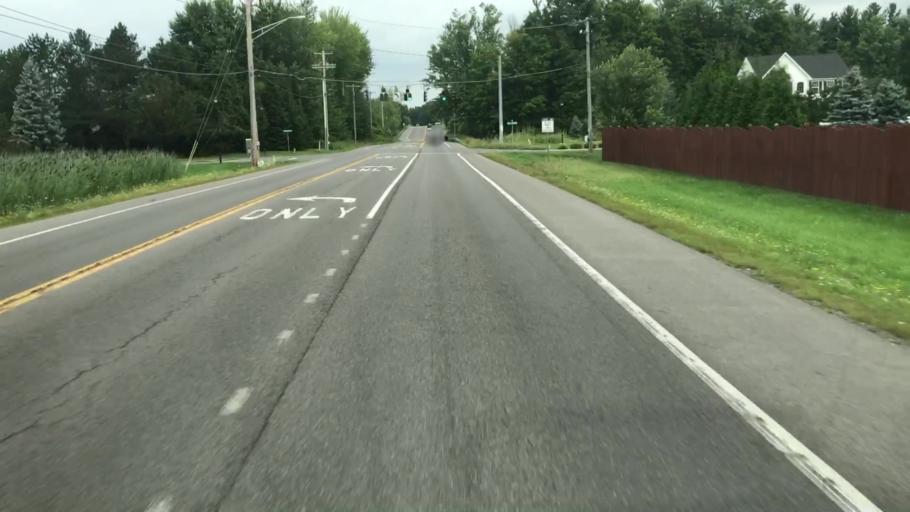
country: US
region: New York
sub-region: Onondaga County
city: Liverpool
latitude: 43.1677
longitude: -76.2089
